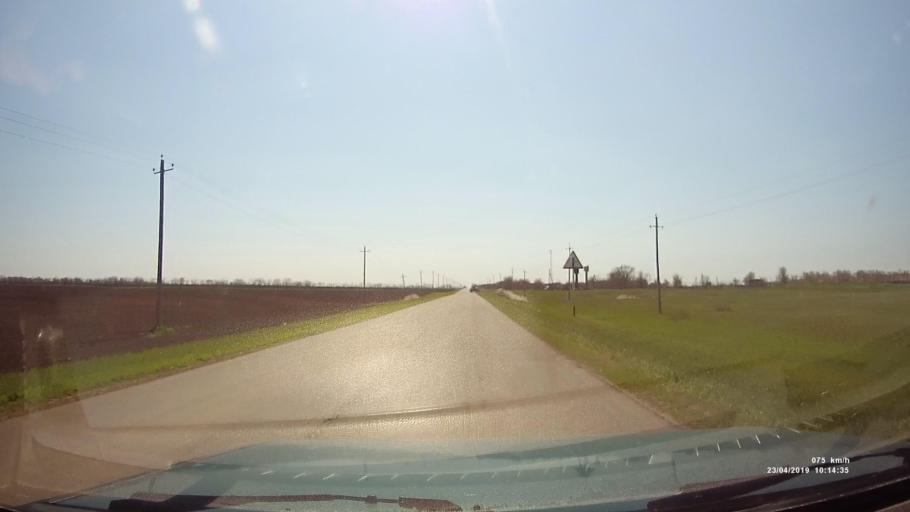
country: RU
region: Rostov
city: Sovetskoye
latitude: 46.6754
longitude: 42.3713
